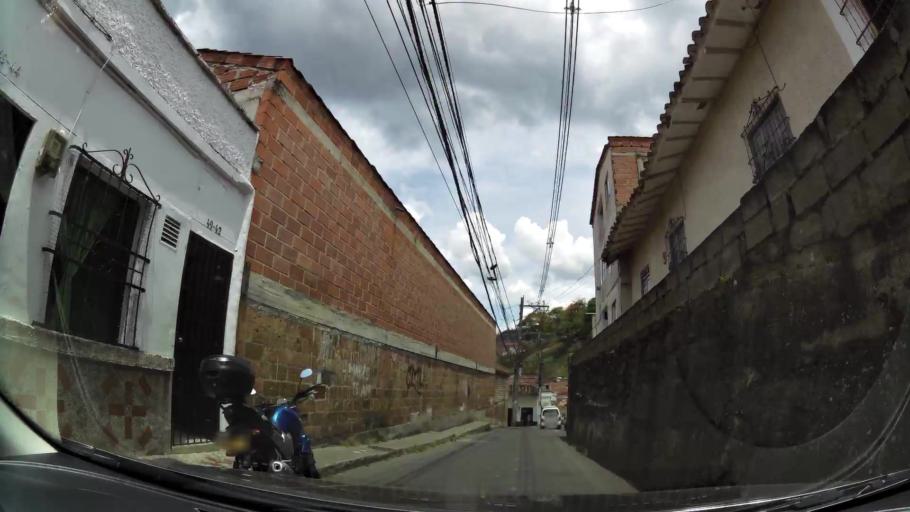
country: CO
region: Antioquia
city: Municipio de Copacabana
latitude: 6.3455
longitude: -75.5071
